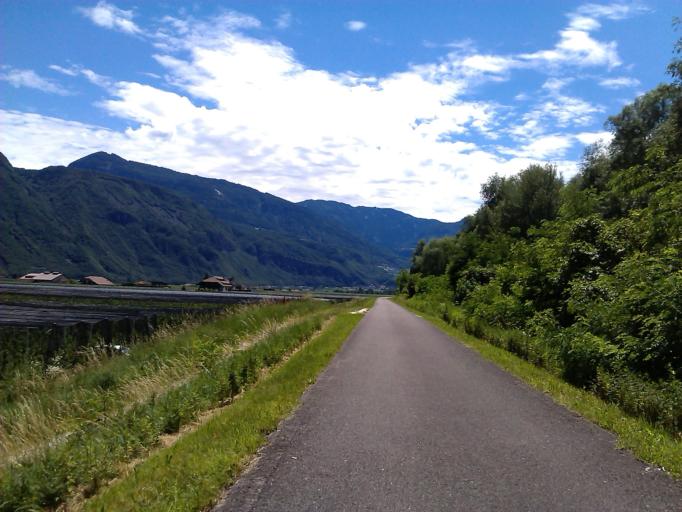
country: IT
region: Trentino-Alto Adige
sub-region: Bolzano
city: Vadena
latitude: 46.3906
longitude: 11.2980
